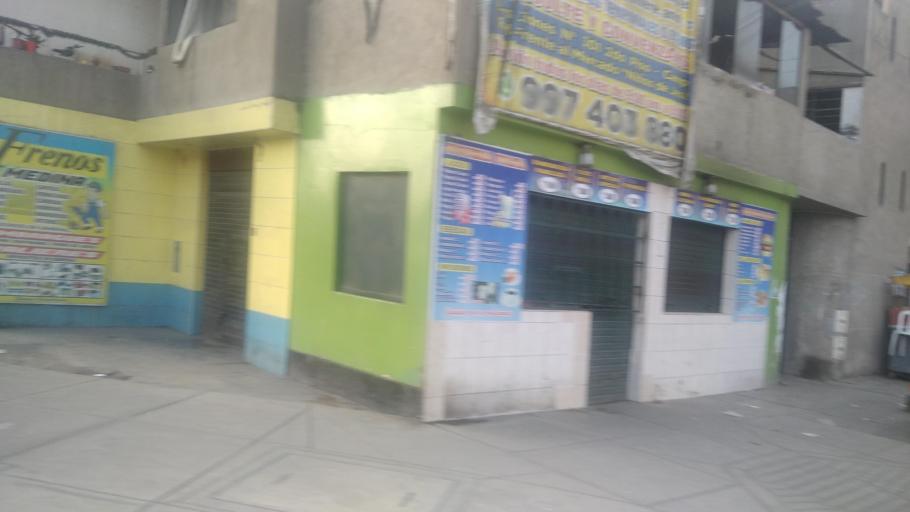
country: PE
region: Lima
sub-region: Lima
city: Vitarte
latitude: -12.0241
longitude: -76.9780
